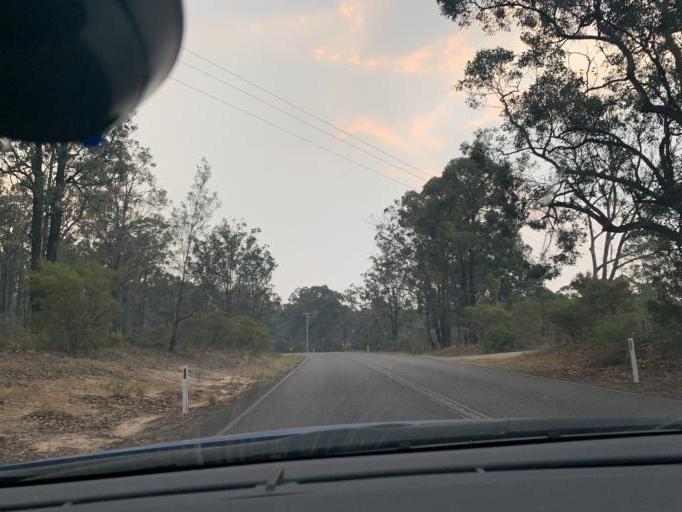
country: AU
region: New South Wales
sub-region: Cessnock
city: Cessnock
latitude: -32.9200
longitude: 151.3409
